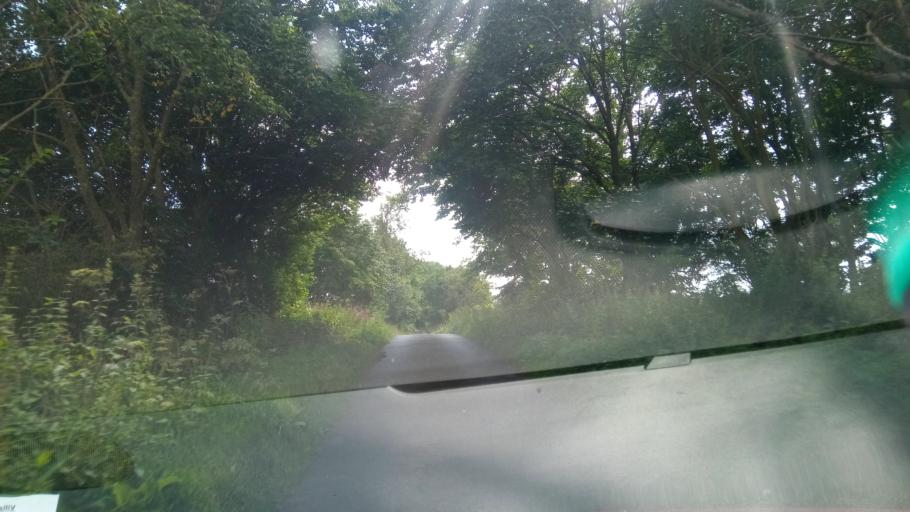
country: GB
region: Scotland
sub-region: The Scottish Borders
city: Jedburgh
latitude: 55.4666
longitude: -2.6394
